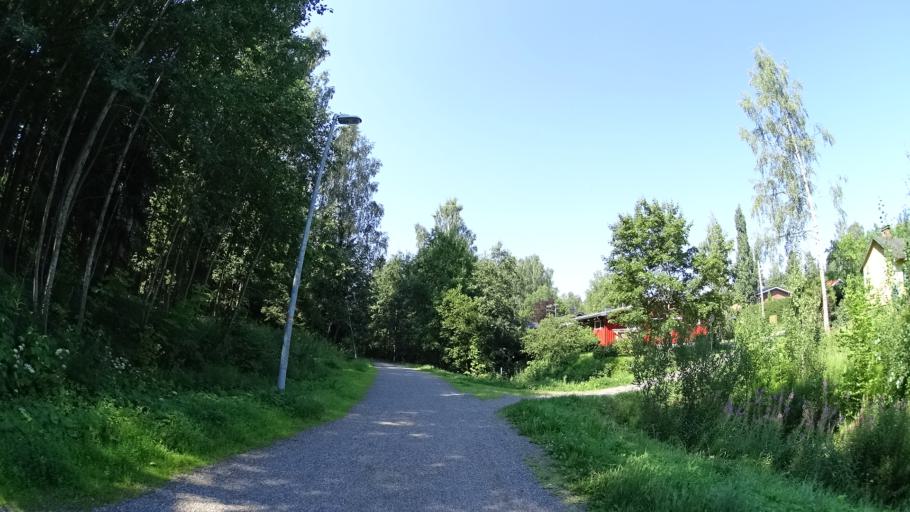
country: FI
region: Uusimaa
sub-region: Helsinki
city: Kerava
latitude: 60.3768
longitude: 25.0875
